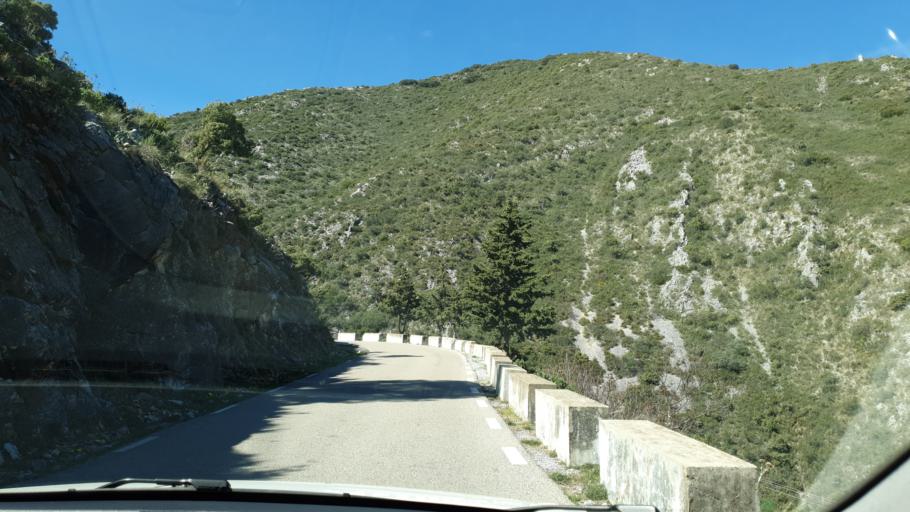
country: ES
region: Andalusia
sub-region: Provincia de Malaga
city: Ojen
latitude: 36.5893
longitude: -4.8792
